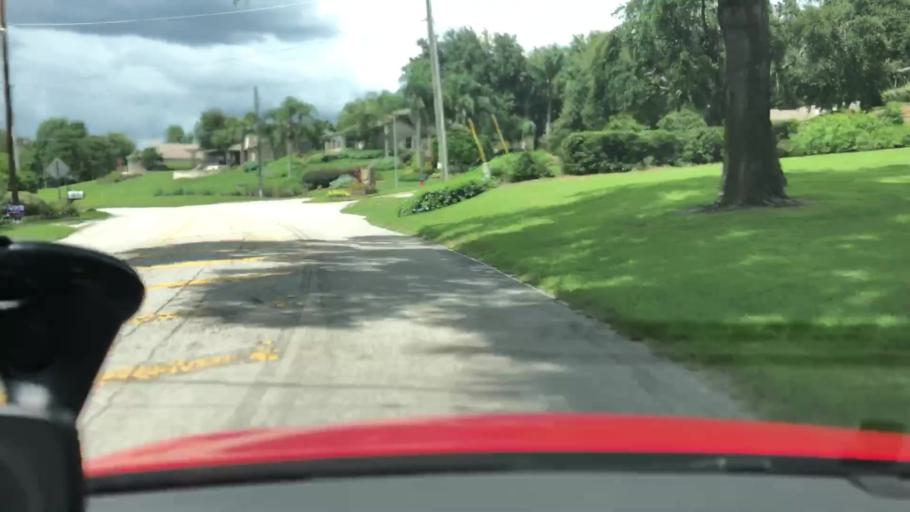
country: US
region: Florida
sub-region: Lake County
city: Mount Dora
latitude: 28.8274
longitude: -81.6574
